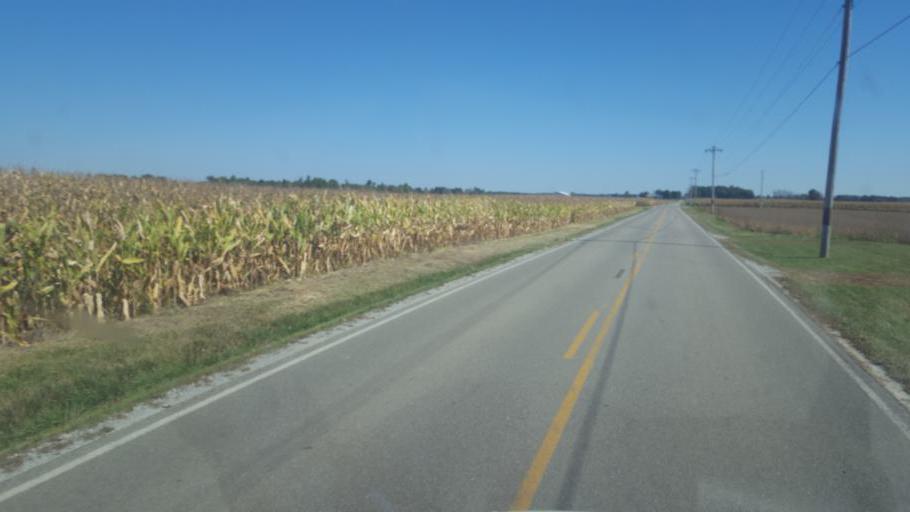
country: US
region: Ohio
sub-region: Huron County
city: Willard
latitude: 40.9820
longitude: -82.7648
